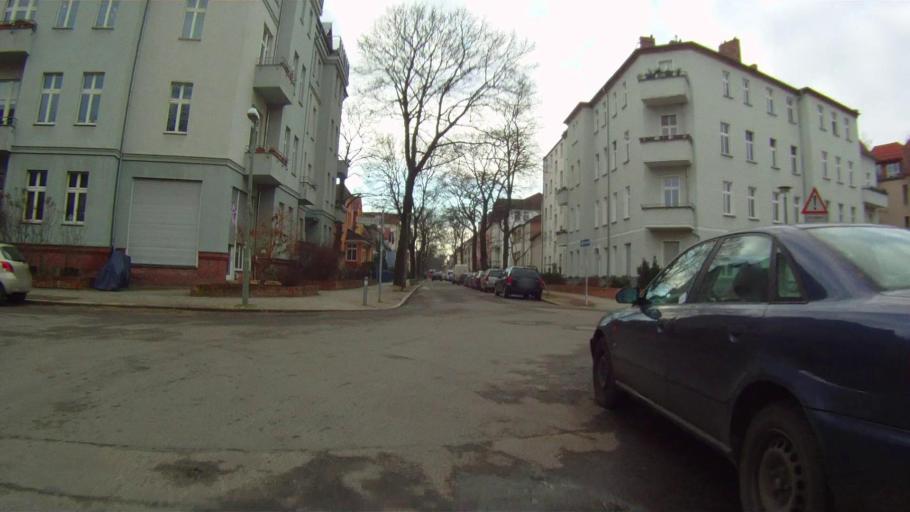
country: DE
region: Berlin
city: Karlshorst
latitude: 52.4894
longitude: 13.5245
